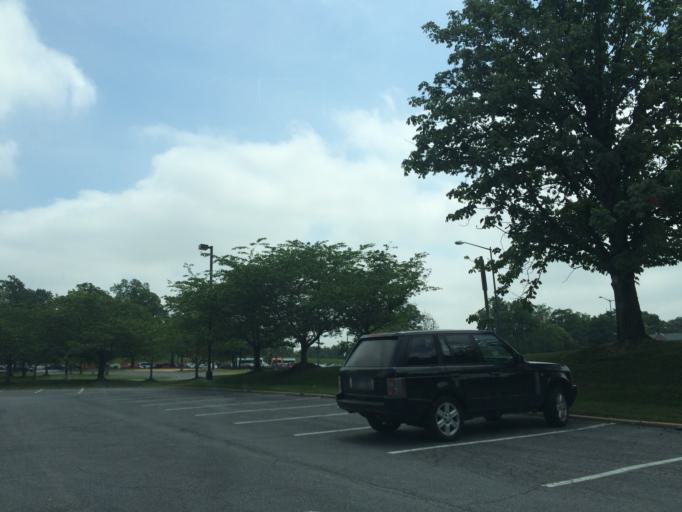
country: US
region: Maryland
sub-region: Prince George's County
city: Chillum
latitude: 38.9317
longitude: -77.0037
